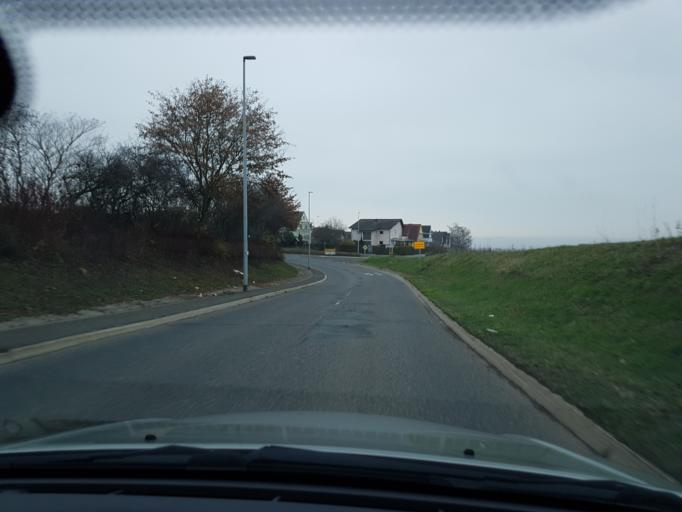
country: DE
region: Hesse
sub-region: Regierungsbezirk Darmstadt
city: Kiedrich
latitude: 50.0380
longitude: 8.0729
